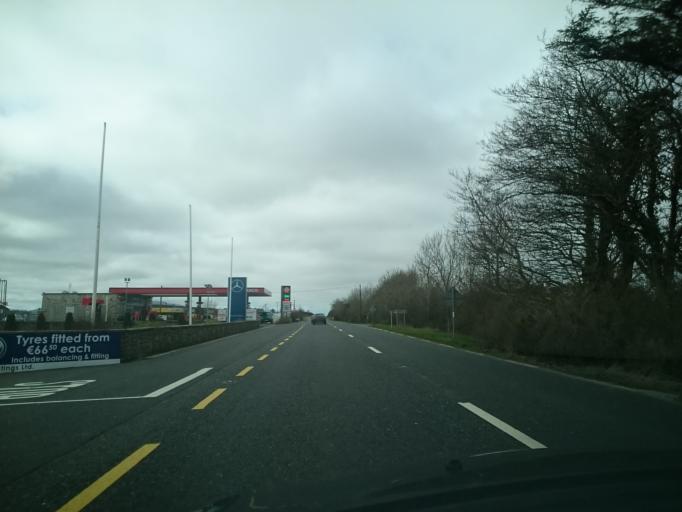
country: IE
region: Connaught
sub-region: Maigh Eo
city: Westport
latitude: 53.8034
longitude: -9.4721
